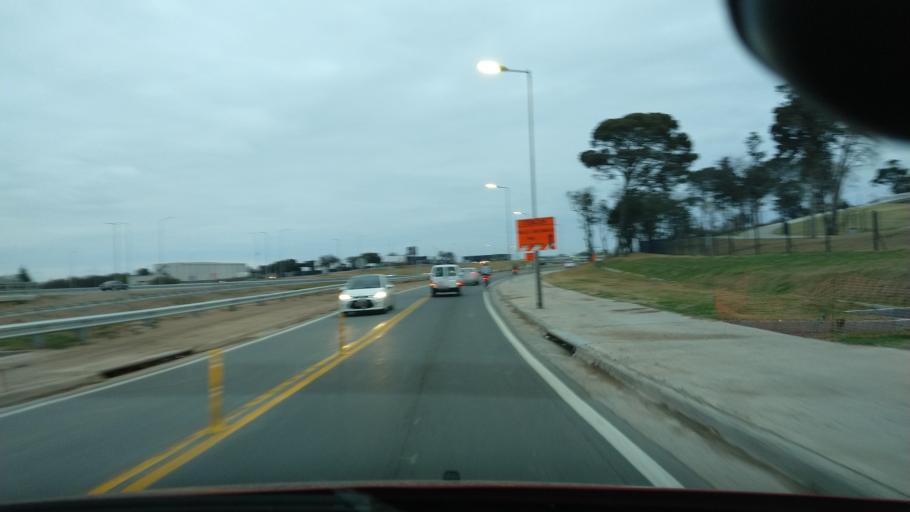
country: AR
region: Cordoba
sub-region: Departamento de Capital
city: Cordoba
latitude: -31.3729
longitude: -64.2534
